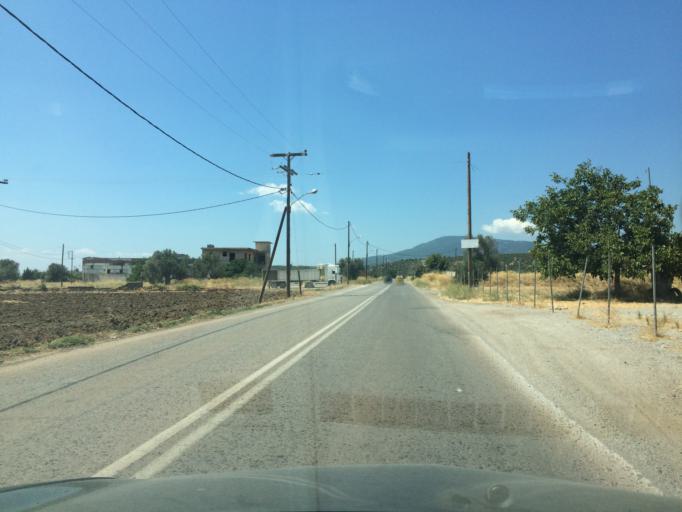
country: GR
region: Central Greece
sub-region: Nomos Evvoias
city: Psachna
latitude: 38.5782
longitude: 23.6285
